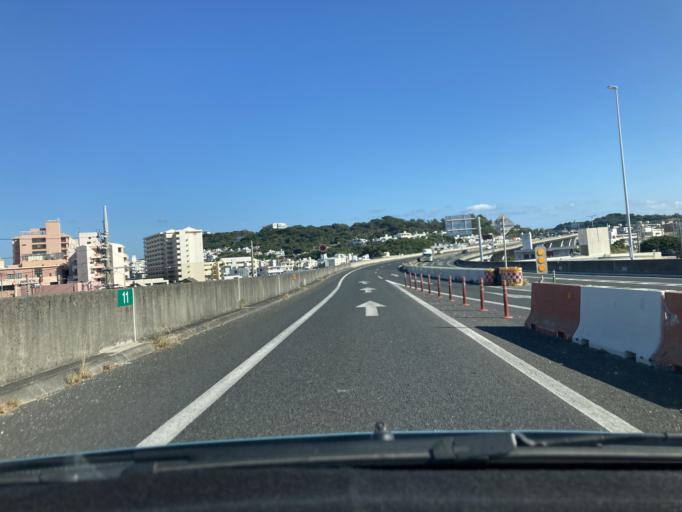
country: JP
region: Okinawa
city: Tomigusuku
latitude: 26.1756
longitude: 127.6731
